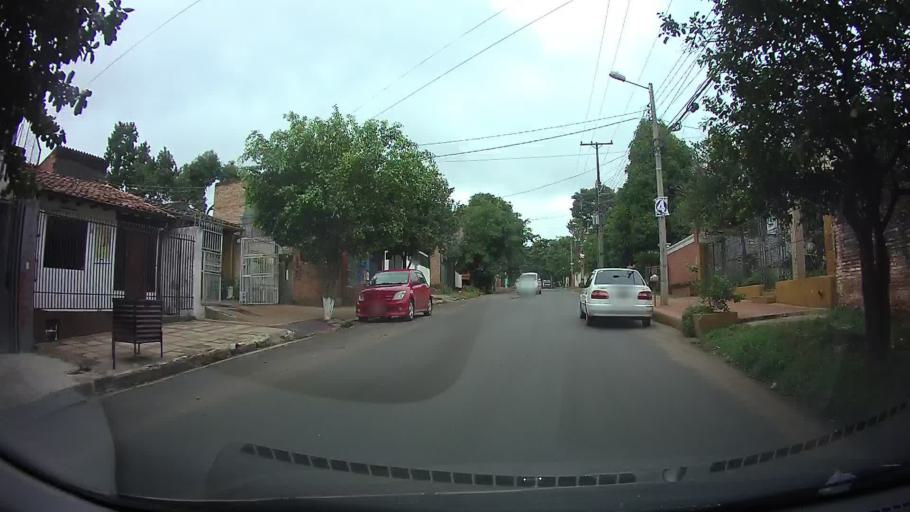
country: PY
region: Central
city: Lambare
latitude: -25.3205
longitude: -57.6123
